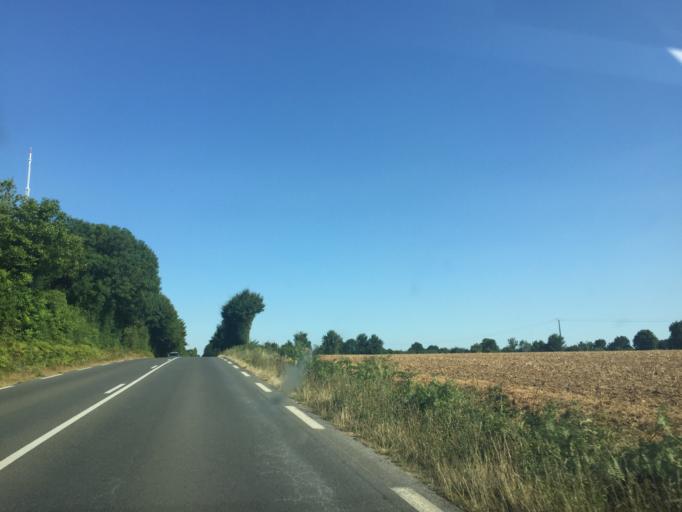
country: FR
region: Poitou-Charentes
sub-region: Departement des Deux-Sevres
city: Melle
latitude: 46.1944
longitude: -0.0656
